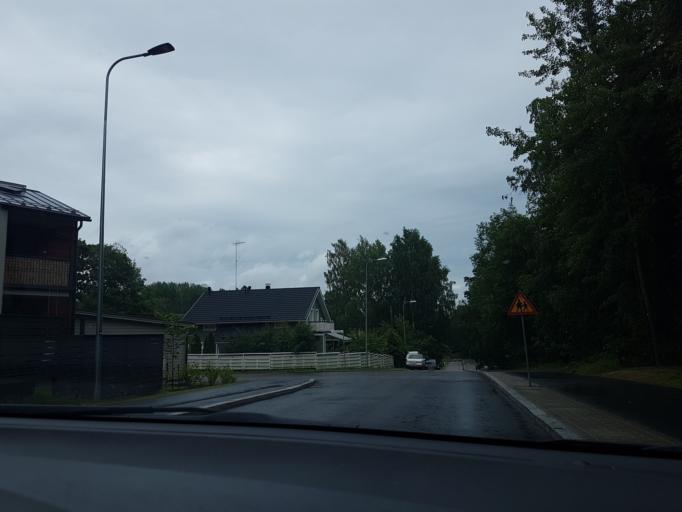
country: FI
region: Uusimaa
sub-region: Helsinki
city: Vantaa
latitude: 60.2347
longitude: 25.1154
